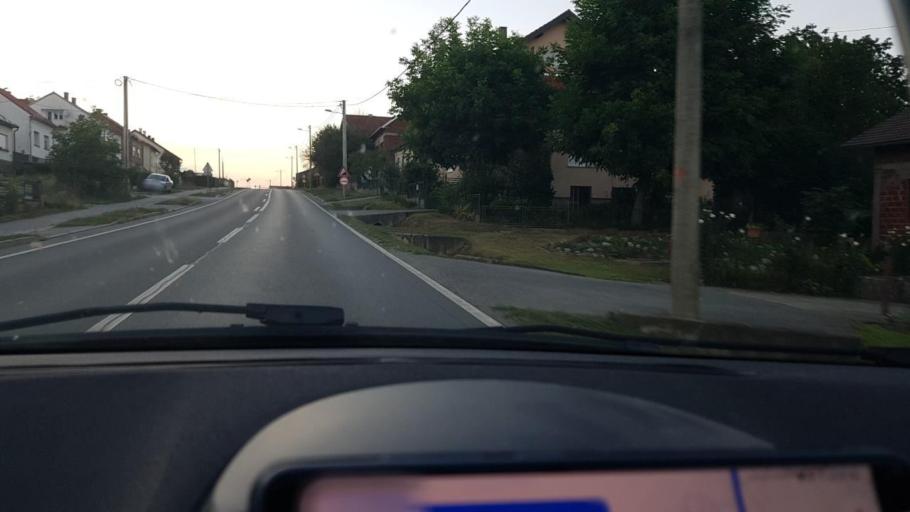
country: HR
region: Bjelovarsko-Bilogorska
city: Zdralovi
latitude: 45.8814
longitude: 16.8680
